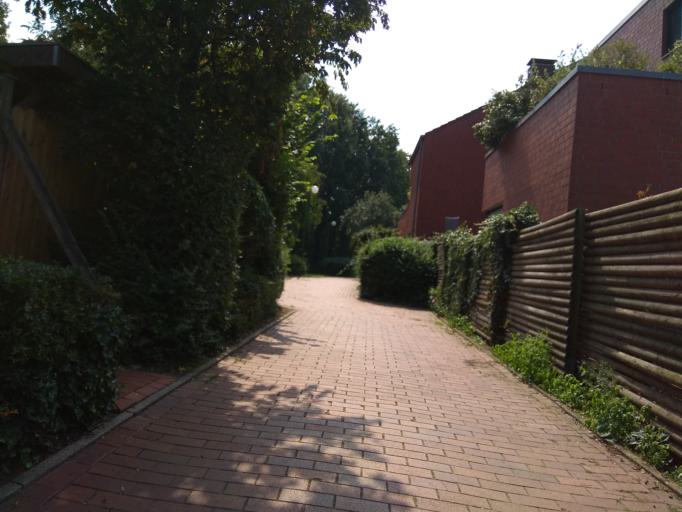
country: DE
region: North Rhine-Westphalia
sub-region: Regierungsbezirk Munster
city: Klein Reken
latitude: 51.7351
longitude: 7.0413
